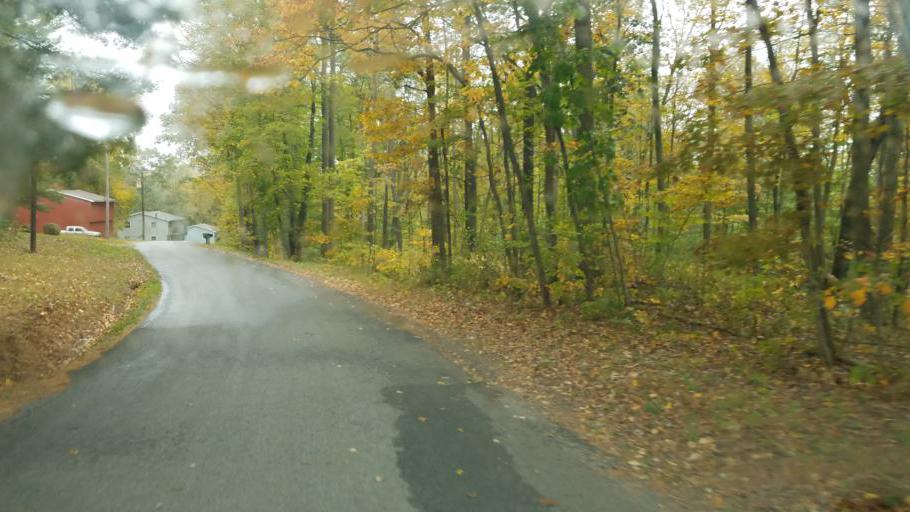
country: US
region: Ohio
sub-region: Holmes County
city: Millersburg
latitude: 40.5654
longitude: -81.8800
